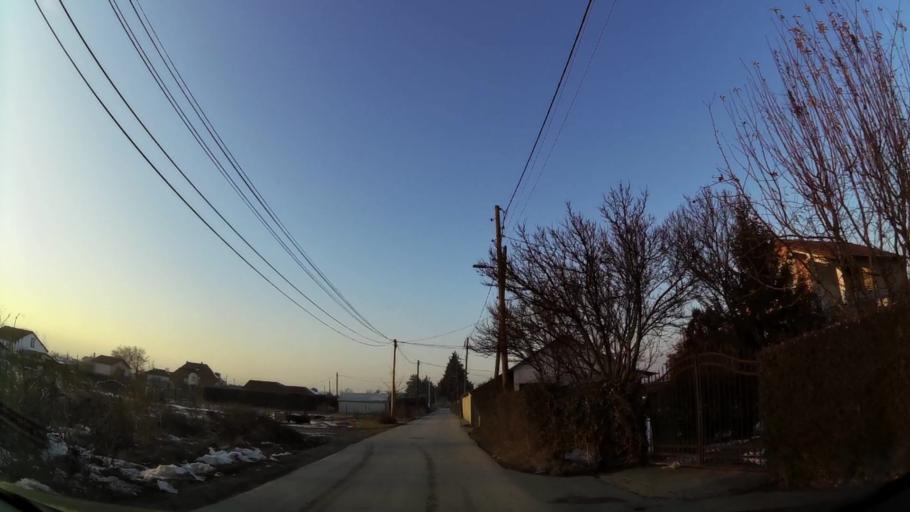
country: MK
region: Kisela Voda
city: Kisela Voda
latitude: 41.9793
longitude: 21.4952
